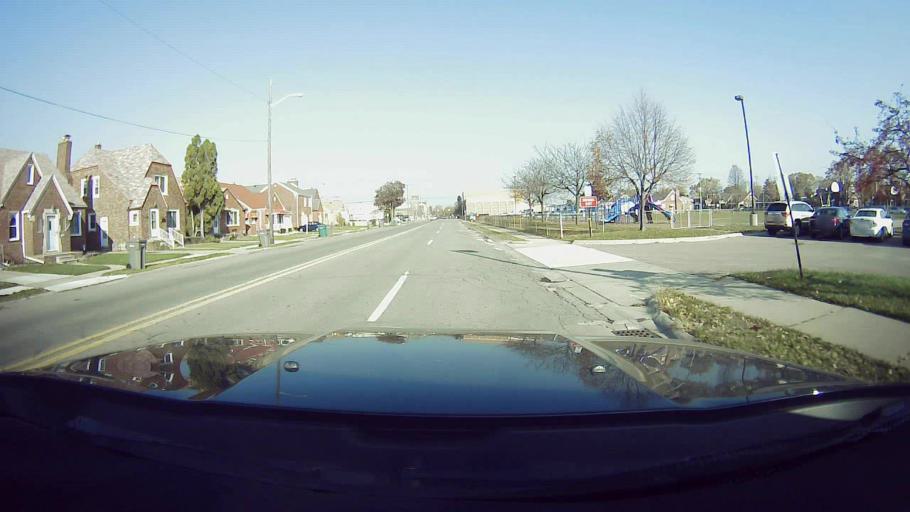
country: US
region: Michigan
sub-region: Wayne County
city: Dearborn
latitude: 42.3416
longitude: -83.1669
